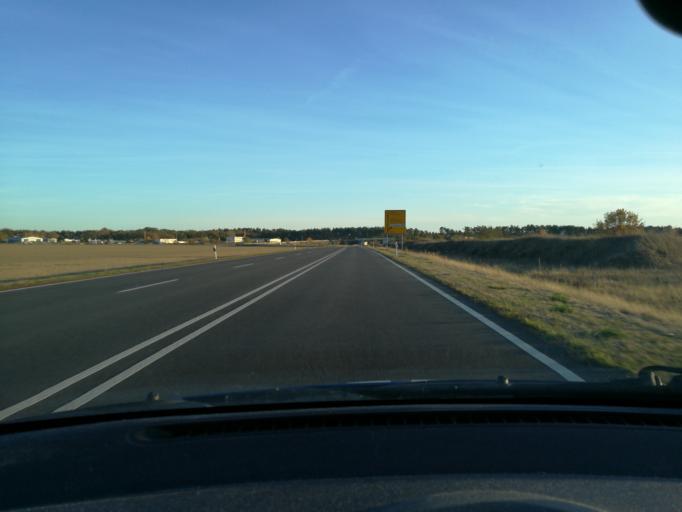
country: DE
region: Brandenburg
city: Perleberg
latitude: 53.0669
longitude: 11.8301
